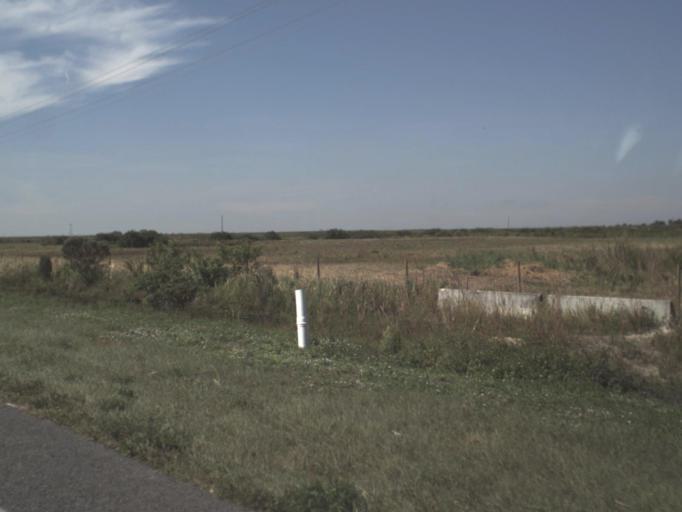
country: US
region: Florida
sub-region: Hendry County
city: Harlem
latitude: 26.7540
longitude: -81.0425
